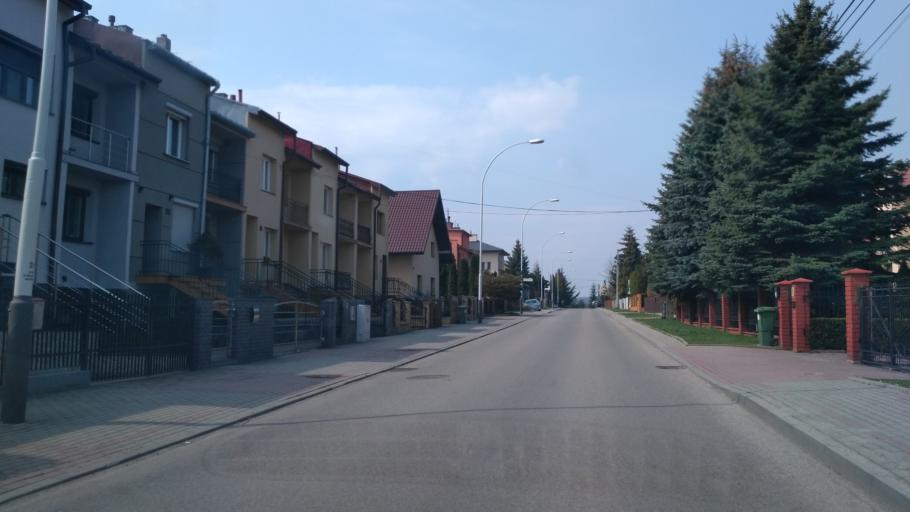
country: PL
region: Subcarpathian Voivodeship
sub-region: Powiat jaroslawski
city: Jaroslaw
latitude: 50.0072
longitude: 22.6643
